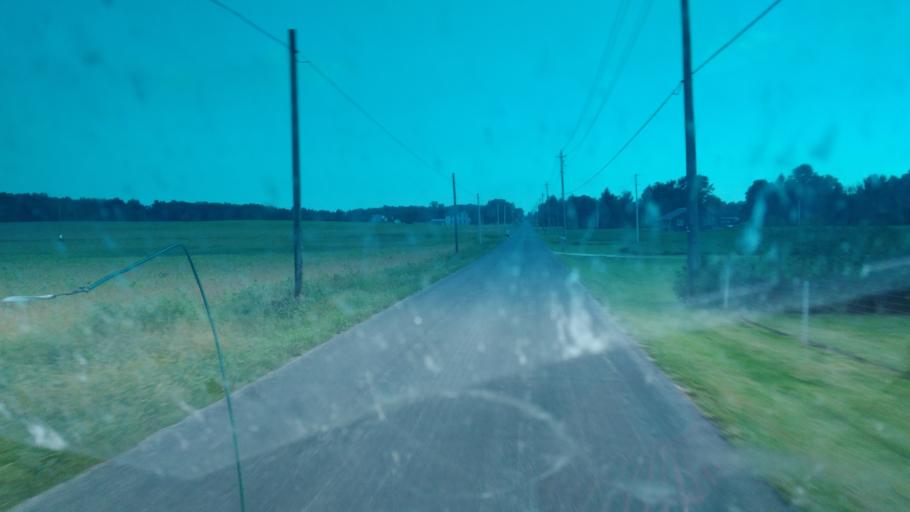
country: US
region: Ohio
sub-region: Crawford County
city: Galion
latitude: 40.7811
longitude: -82.8195
